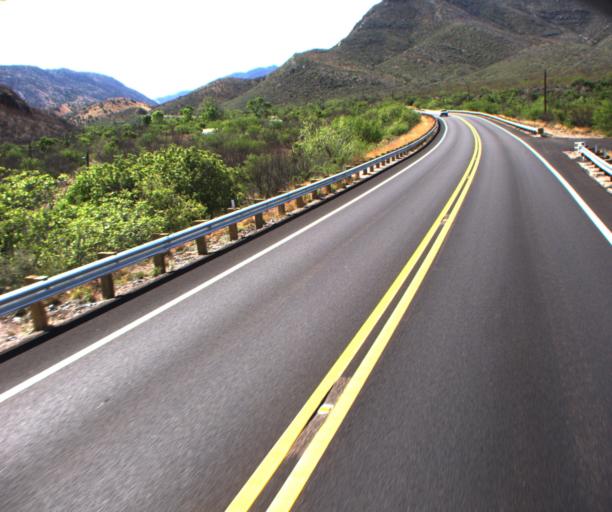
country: US
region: Arizona
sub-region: Cochise County
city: Bisbee
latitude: 31.5131
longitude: -110.0180
